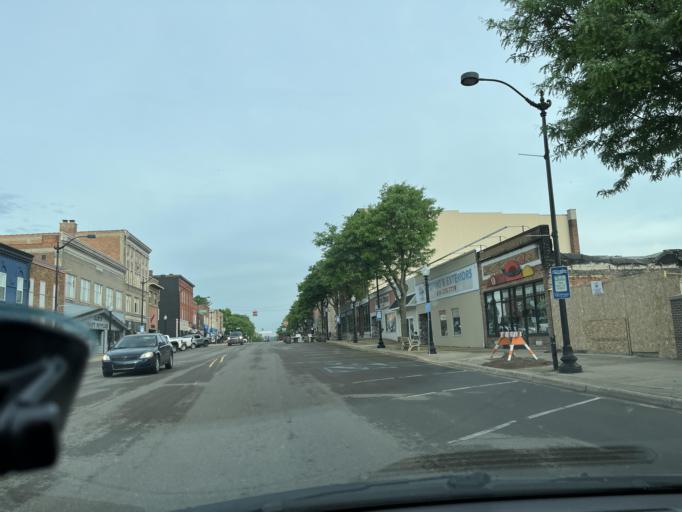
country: US
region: Michigan
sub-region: Barry County
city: Hastings
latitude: 42.6489
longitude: -85.2864
